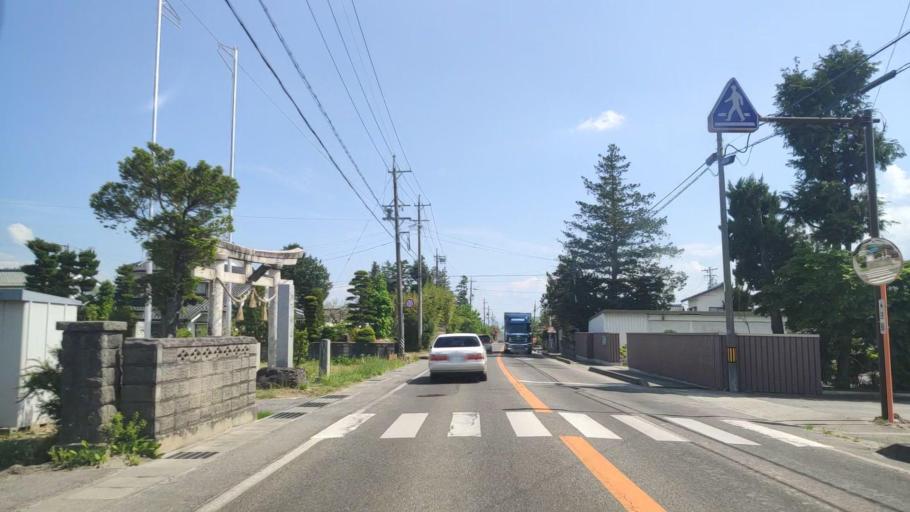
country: JP
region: Nagano
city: Hotaka
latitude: 36.3947
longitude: 137.8633
